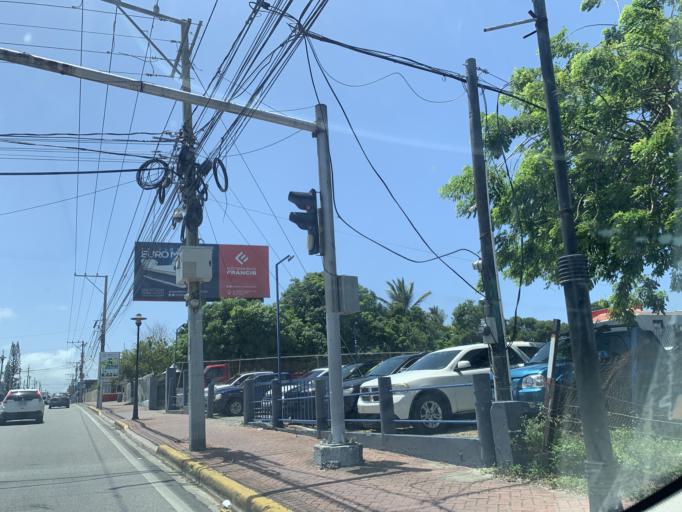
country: DO
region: Puerto Plata
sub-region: Puerto Plata
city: Puerto Plata
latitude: 19.7837
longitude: -70.6779
